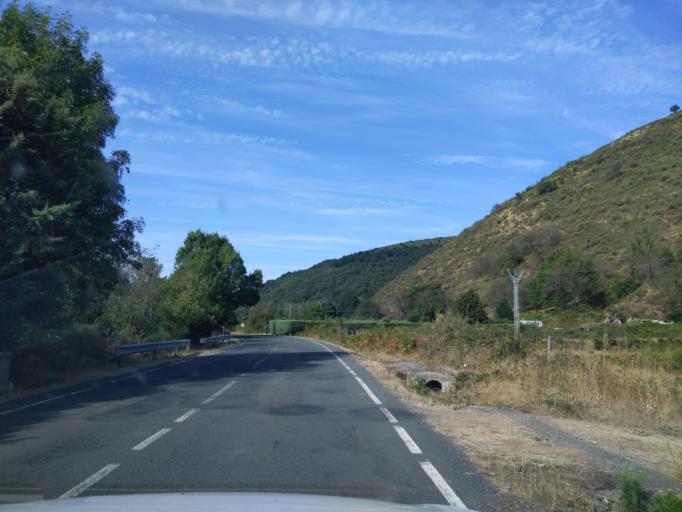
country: ES
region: La Rioja
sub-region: Provincia de La Rioja
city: Ezcaray
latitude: 42.2885
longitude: -3.0262
